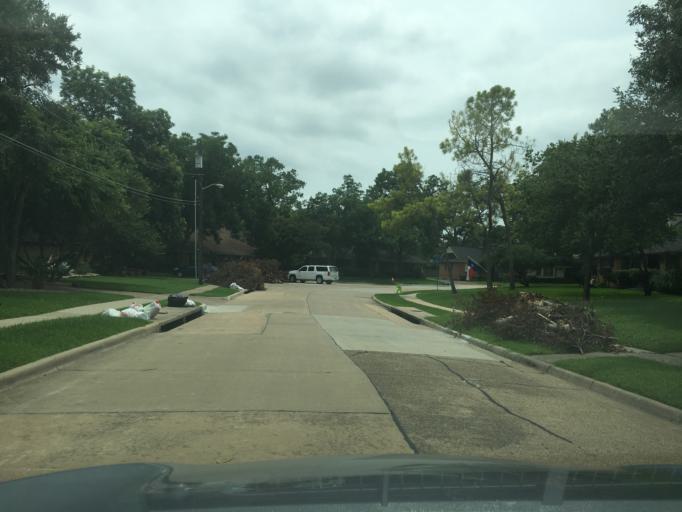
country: US
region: Texas
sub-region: Dallas County
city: Richardson
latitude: 32.9448
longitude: -96.7556
